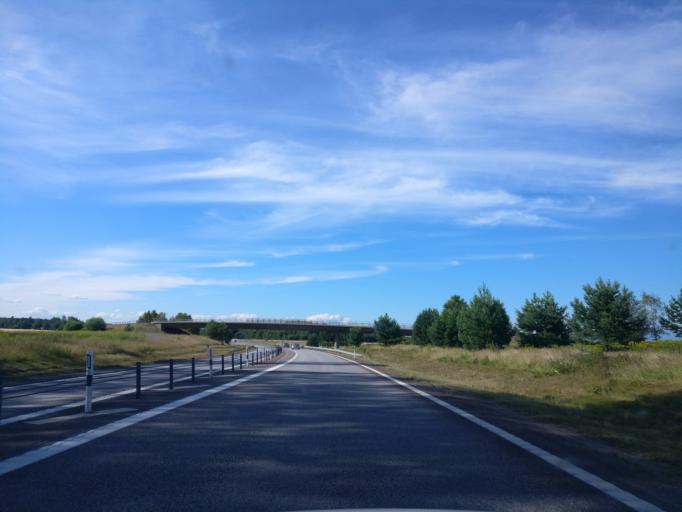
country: SE
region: Vaermland
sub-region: Karlstads Kommun
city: Karlstad
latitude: 59.4287
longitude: 13.4084
